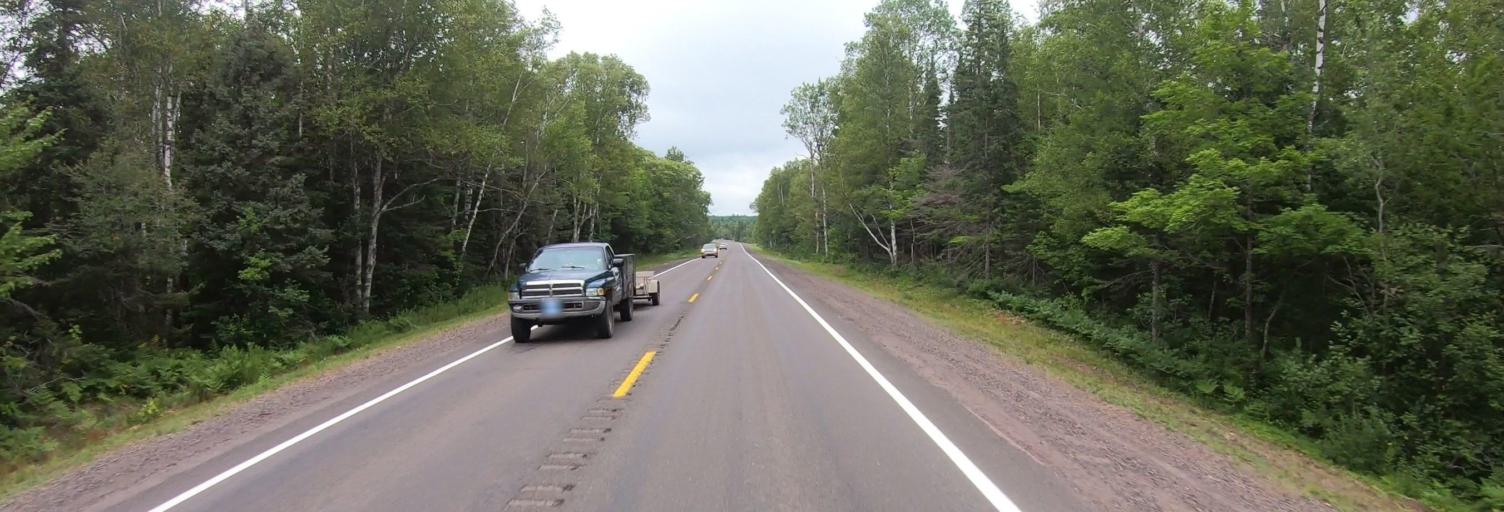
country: US
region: Michigan
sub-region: Keweenaw County
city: Eagle River
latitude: 47.3349
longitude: -88.3230
